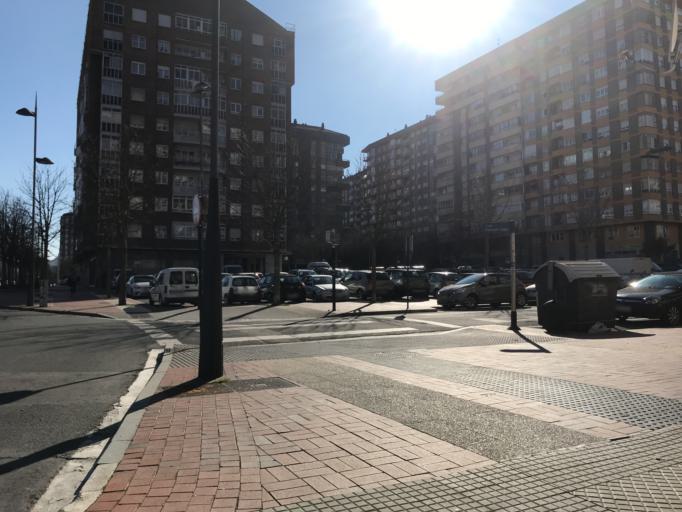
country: ES
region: Basque Country
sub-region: Provincia de Alava
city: Gasteiz / Vitoria
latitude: 42.8463
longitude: -2.6584
